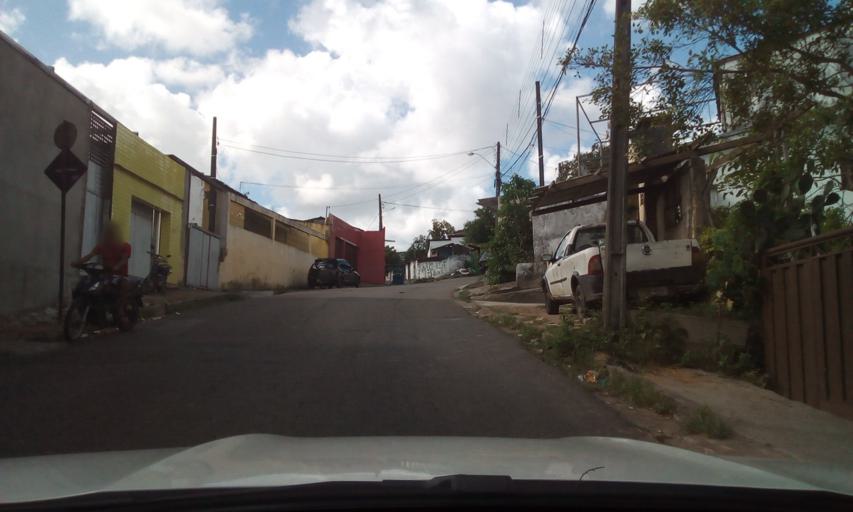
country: BR
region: Paraiba
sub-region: Joao Pessoa
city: Joao Pessoa
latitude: -7.1290
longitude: -34.8862
